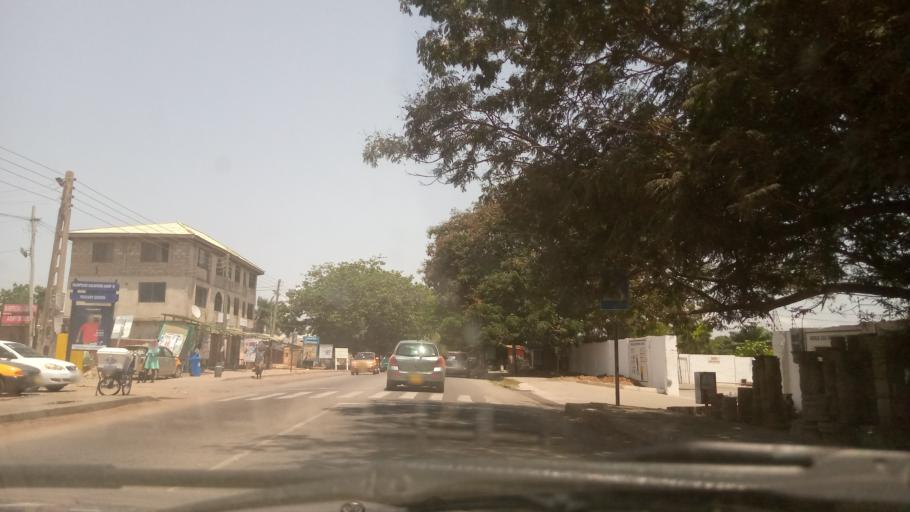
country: GH
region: Greater Accra
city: Accra
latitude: 5.5413
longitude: -0.2393
